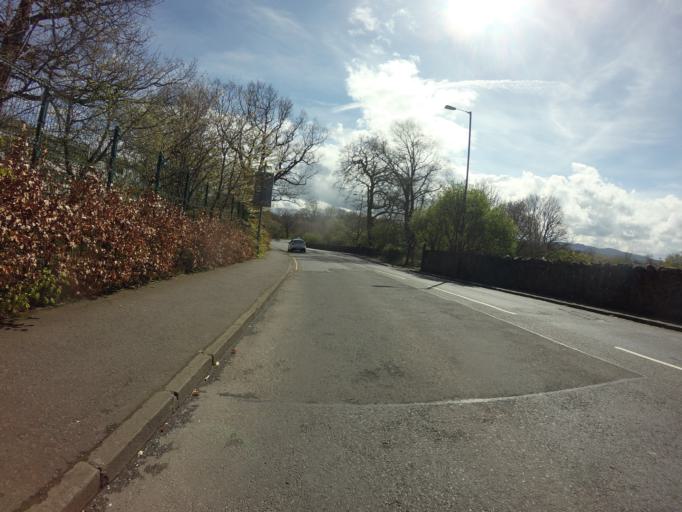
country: GB
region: Scotland
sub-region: West Lothian
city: Seafield
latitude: 55.9411
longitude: -3.1454
